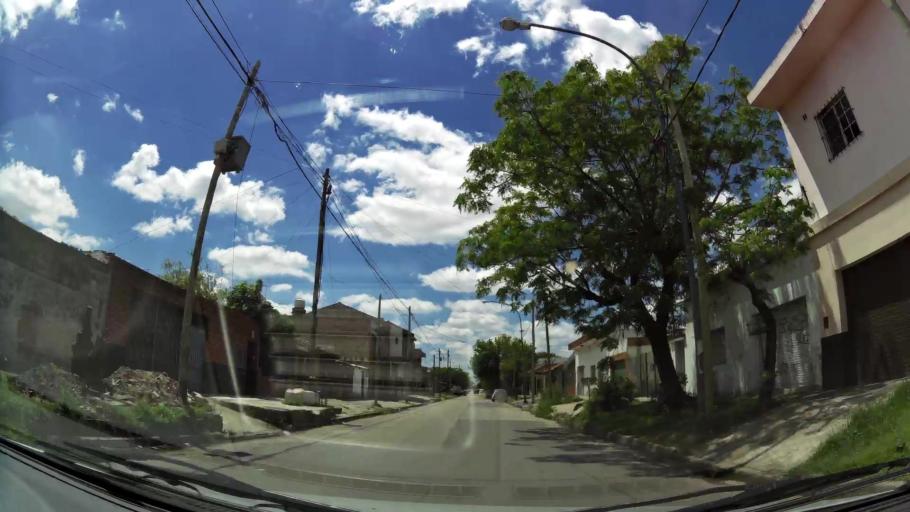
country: AR
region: Buenos Aires
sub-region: Partido de Lanus
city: Lanus
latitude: -34.7059
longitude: -58.4268
